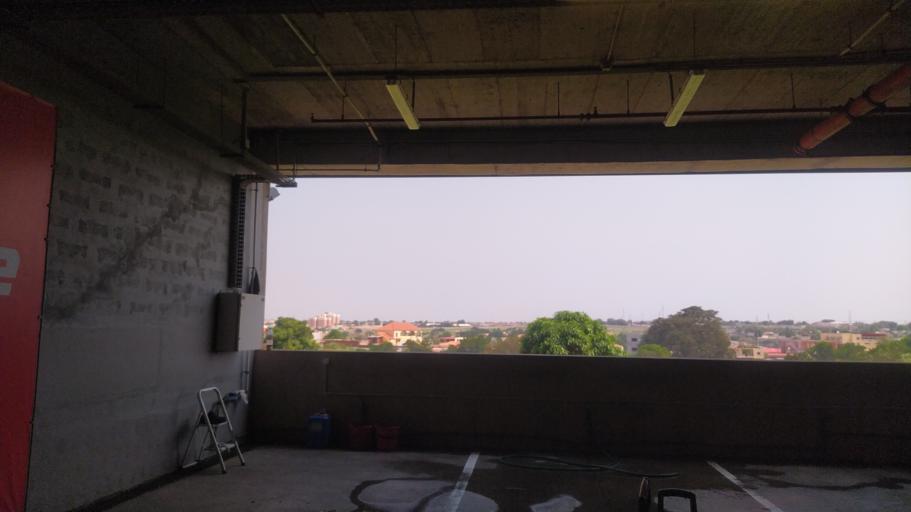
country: AO
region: Luanda
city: Luanda
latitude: -8.8971
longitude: 13.2249
